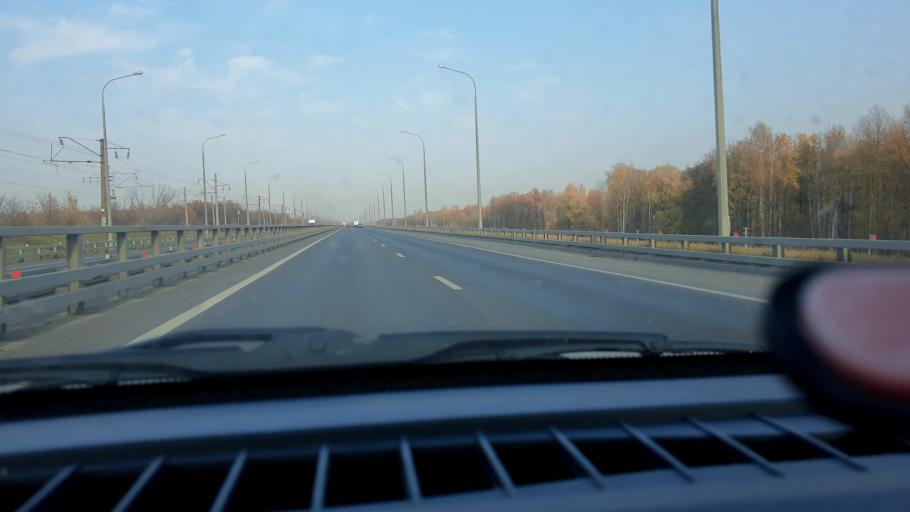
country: RU
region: Nizjnij Novgorod
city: Neklyudovo
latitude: 56.3745
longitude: 43.9513
